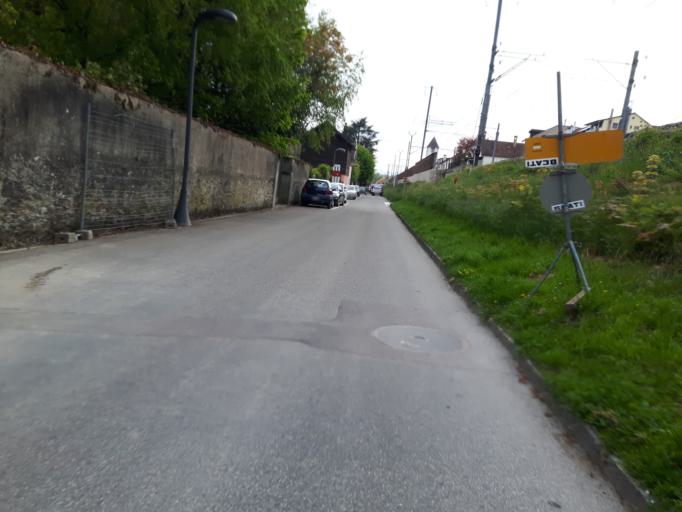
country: CH
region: Vaud
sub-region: Jura-Nord vaudois District
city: Grandson
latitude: 46.8086
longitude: 6.6465
